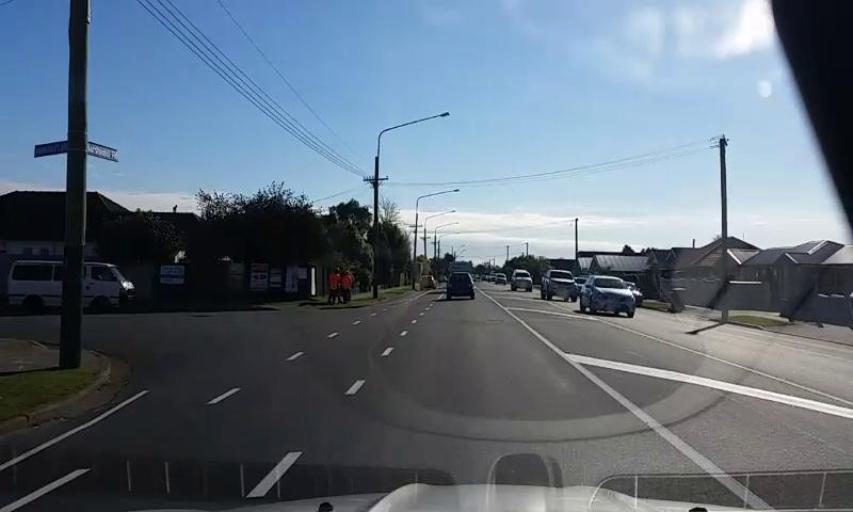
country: NZ
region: Canterbury
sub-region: Christchurch City
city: Christchurch
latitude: -43.5032
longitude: 172.6623
